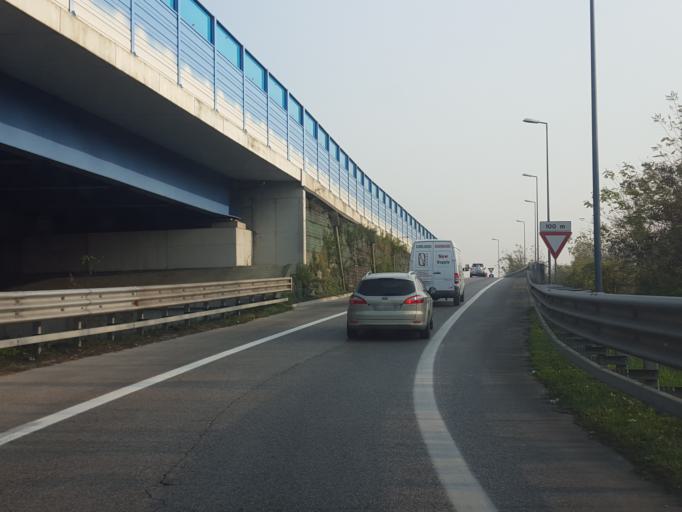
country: IT
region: Veneto
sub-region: Provincia di Treviso
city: Treviso
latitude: 45.6555
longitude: 12.2111
